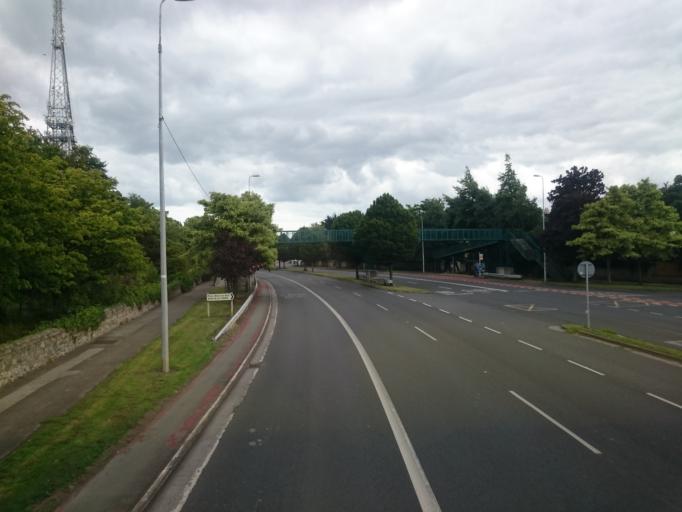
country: IE
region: Leinster
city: Donnybrook
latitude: 53.3152
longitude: -6.2263
